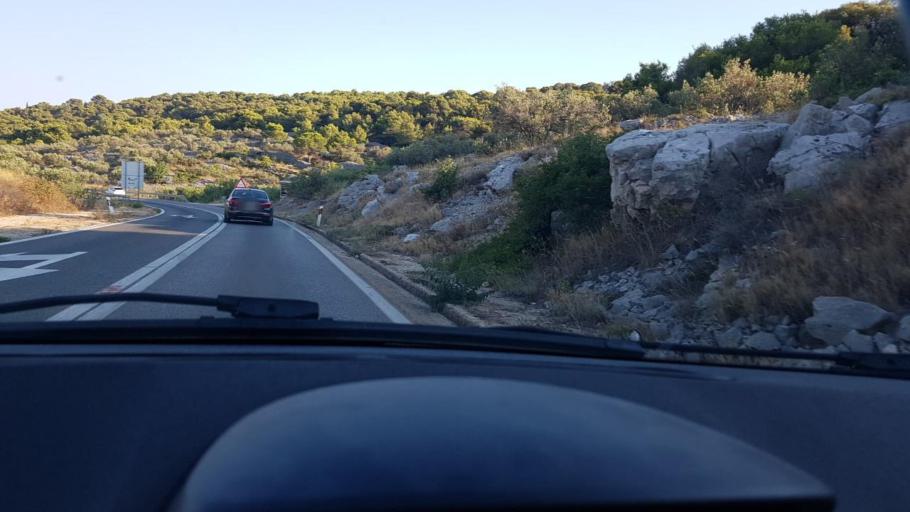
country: HR
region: Sibensko-Kniniska
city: Murter
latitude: 43.8108
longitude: 15.6023
